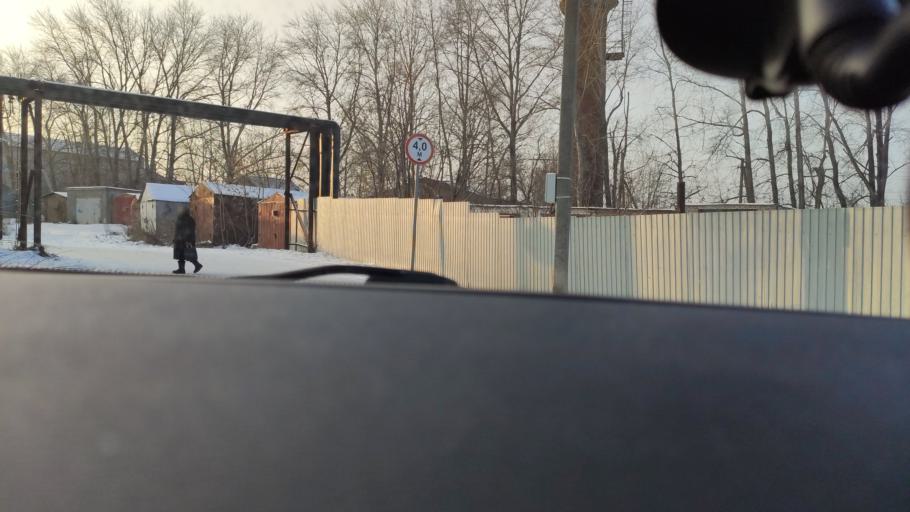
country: RU
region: Perm
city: Kondratovo
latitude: 57.9443
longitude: 56.0623
